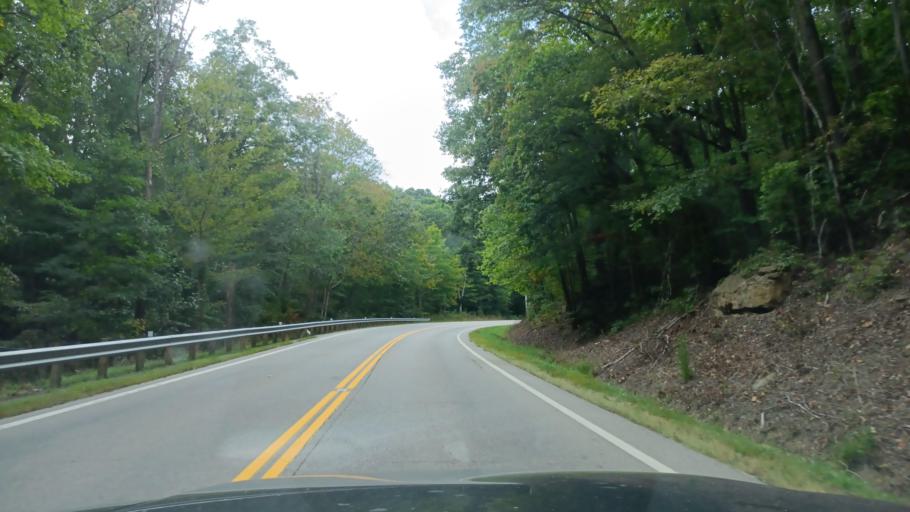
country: US
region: Ohio
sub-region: Vinton County
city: McArthur
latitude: 39.2361
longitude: -82.3344
